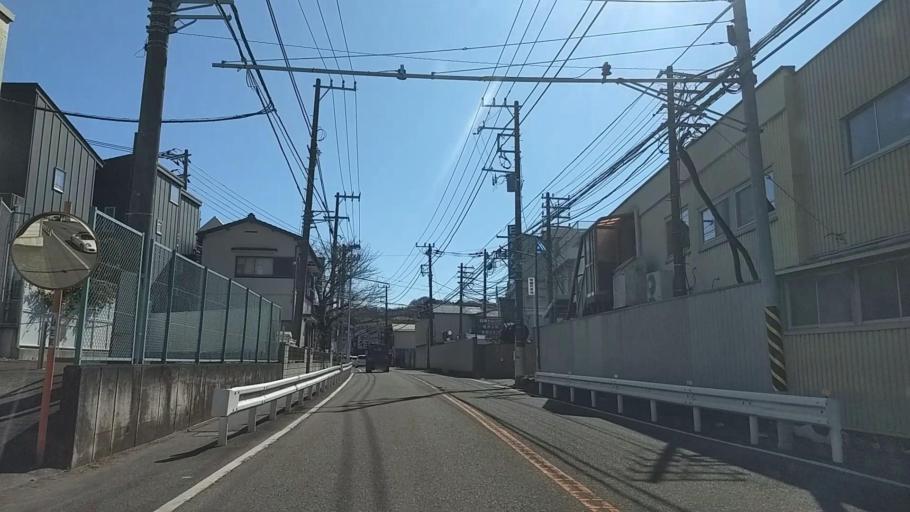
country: JP
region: Kanagawa
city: Kamakura
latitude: 35.3246
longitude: 139.5245
